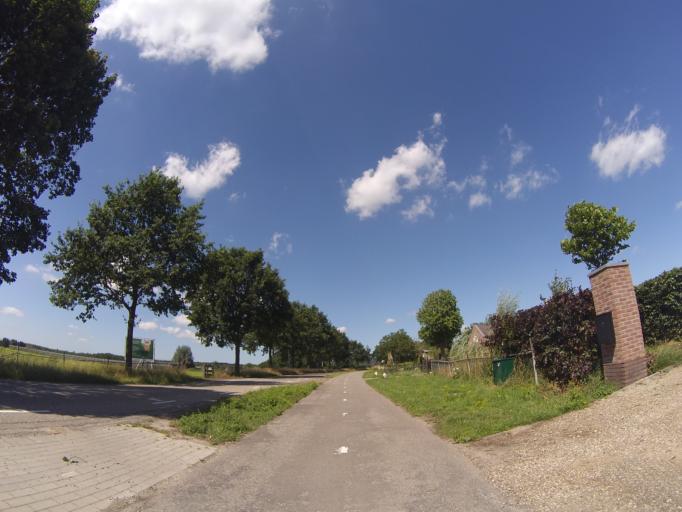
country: NL
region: Utrecht
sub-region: Stichtse Vecht
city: Spechtenkamp
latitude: 52.1148
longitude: 5.0120
